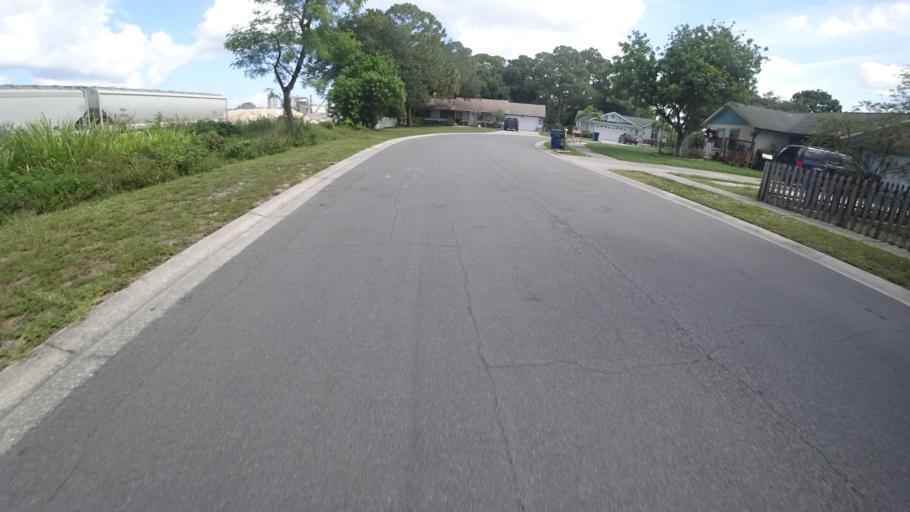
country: US
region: Florida
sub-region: Manatee County
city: Samoset
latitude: 27.4545
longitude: -82.5432
